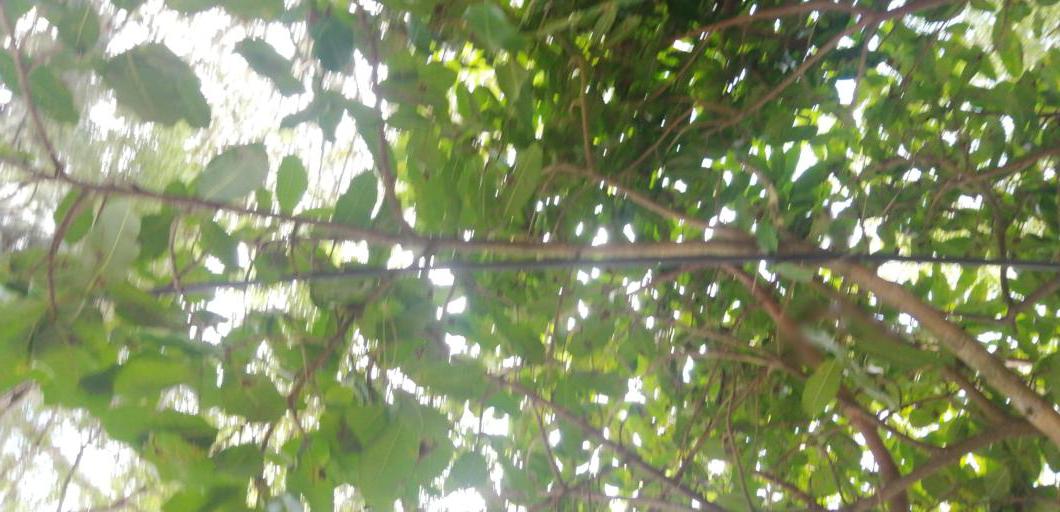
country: CR
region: Guanacaste
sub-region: Canton de Tilaran
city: Tilaran
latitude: 10.4700
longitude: -84.9680
